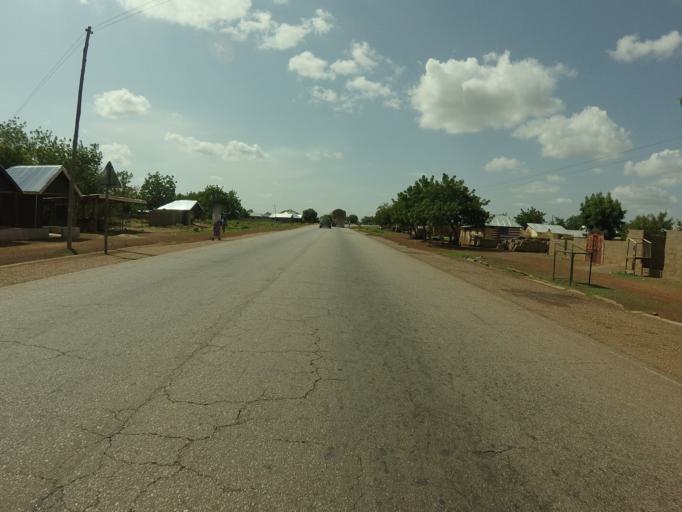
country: GH
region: Northern
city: Savelugu
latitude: 9.8733
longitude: -0.8721
